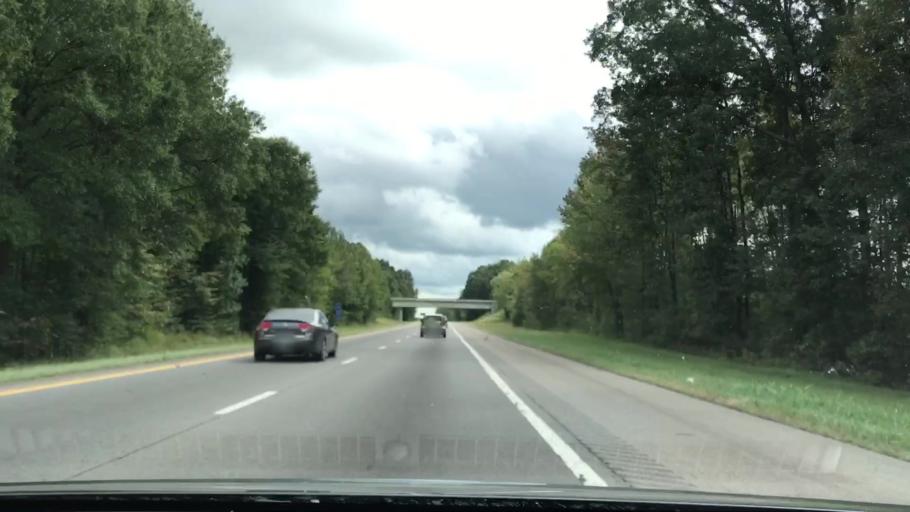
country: US
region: Tennessee
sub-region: Cheatham County
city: Pleasant View
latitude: 36.4104
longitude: -87.0399
